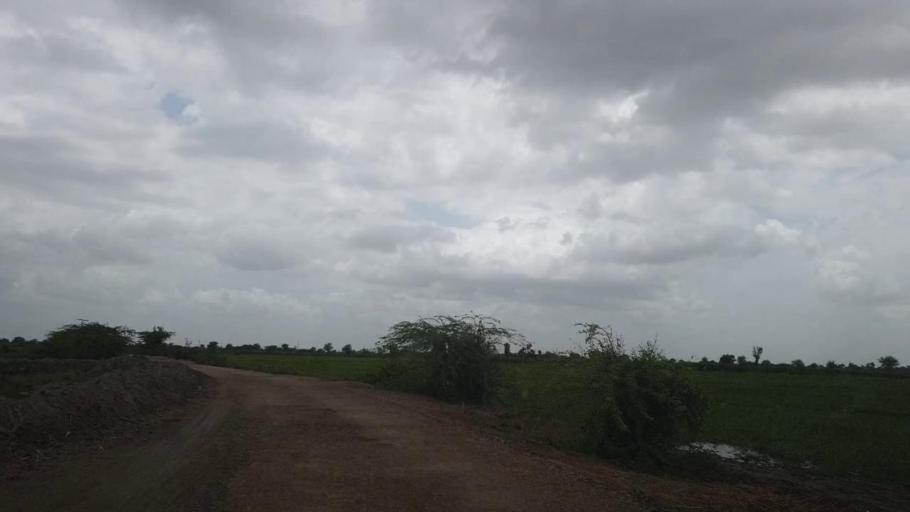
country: PK
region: Sindh
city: Badin
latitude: 24.6534
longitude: 68.9459
